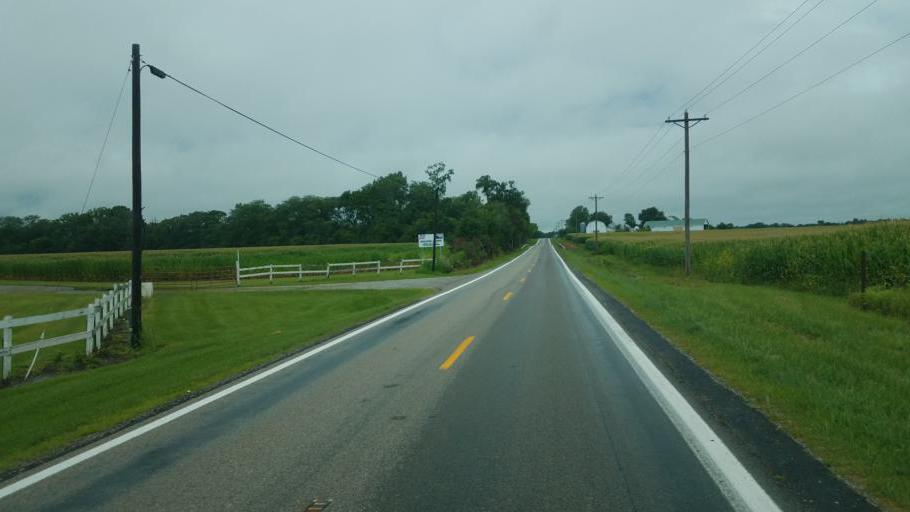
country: US
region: Ohio
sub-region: Union County
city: Richwood
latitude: 40.5447
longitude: -83.3624
